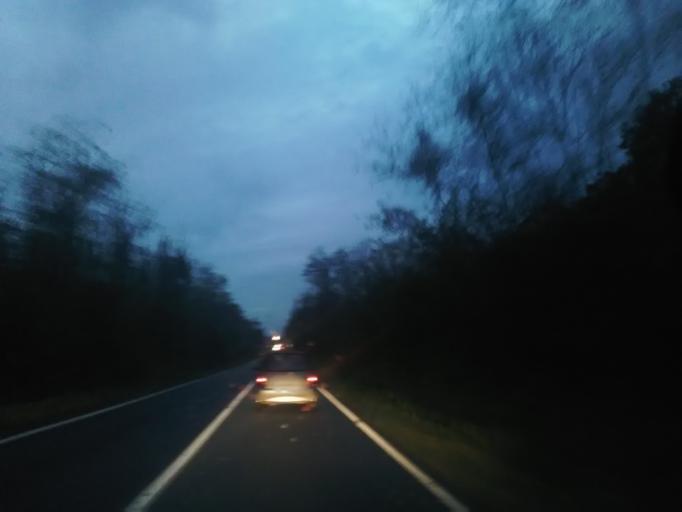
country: IT
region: Piedmont
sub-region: Provincia di Vercelli
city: Lozzolo
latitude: 45.6100
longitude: 8.3344
